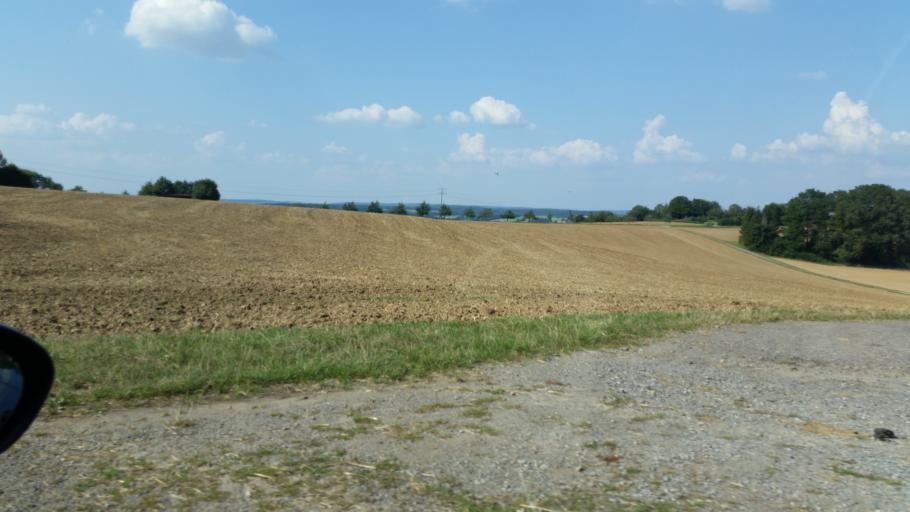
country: DE
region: Baden-Wuerttemberg
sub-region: Karlsruhe Region
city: Osterburken
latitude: 49.4292
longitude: 9.4492
